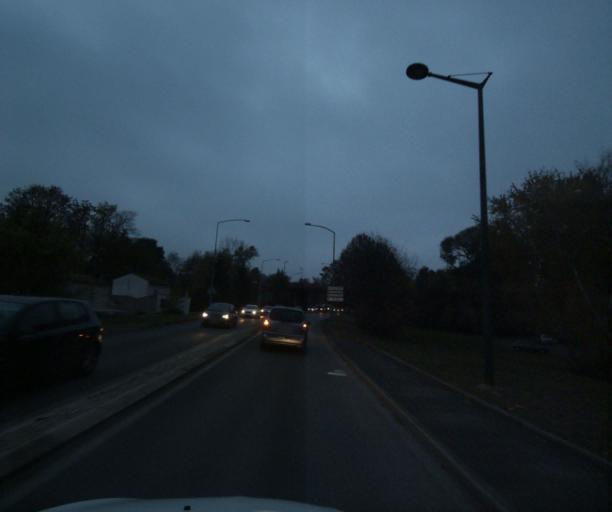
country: FR
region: Poitou-Charentes
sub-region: Departement de la Charente-Maritime
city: Saintes
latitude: 45.7417
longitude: -0.6396
